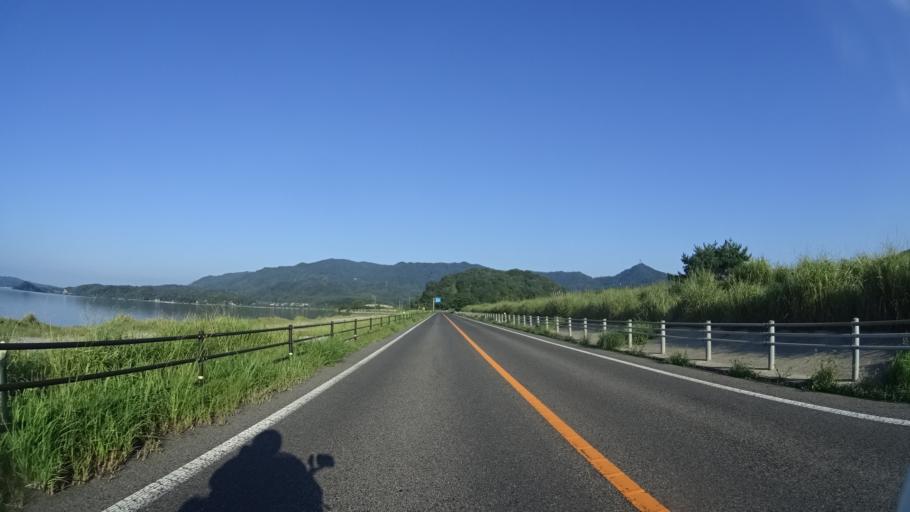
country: JP
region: Shimane
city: Sakaiminato
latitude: 35.5297
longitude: 133.1670
